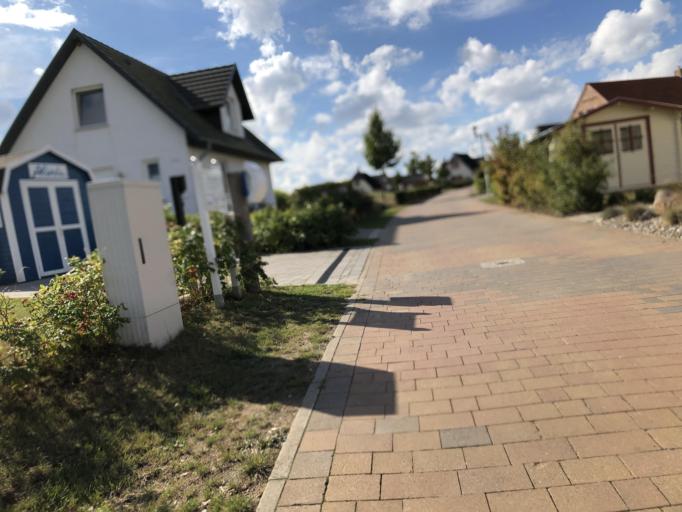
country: DE
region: Mecklenburg-Vorpommern
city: Gramkow
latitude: 53.9308
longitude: 11.3825
